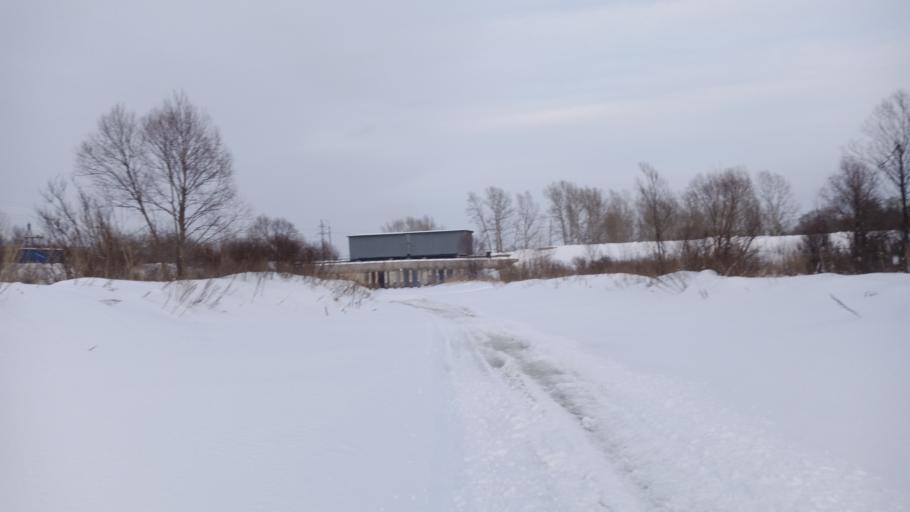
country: RU
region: Altai Krai
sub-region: Gorod Barnaulskiy
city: Barnaul
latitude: 53.3109
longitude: 83.7321
